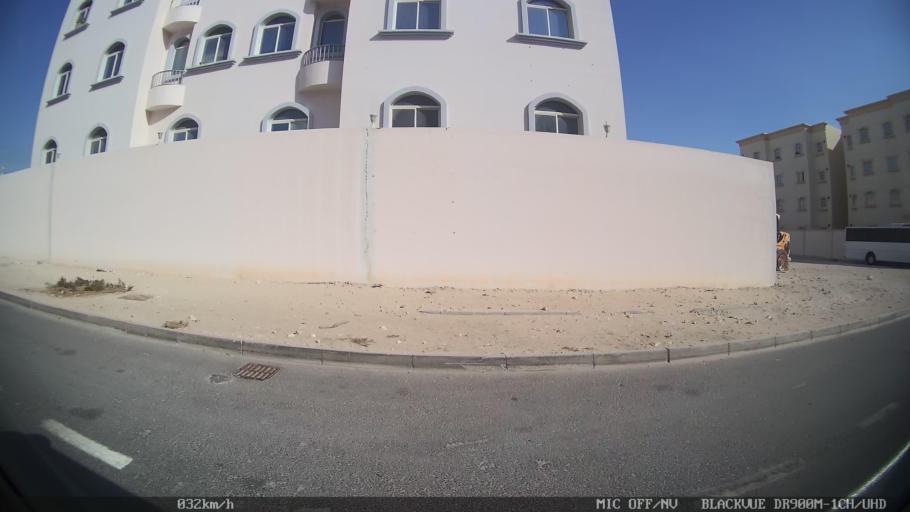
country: QA
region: Al Wakrah
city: Al Wakrah
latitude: 25.1651
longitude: 51.6021
